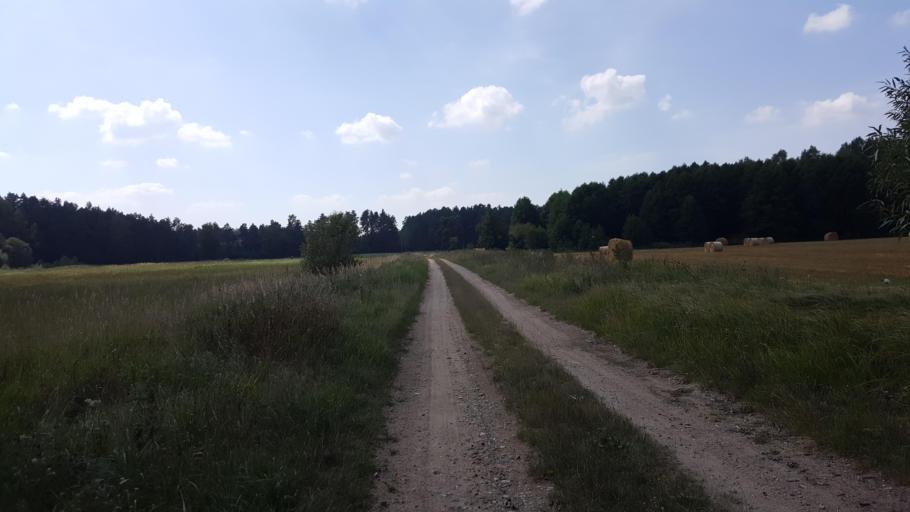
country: PL
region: Podlasie
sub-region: Powiat hajnowski
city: Hajnowka
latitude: 52.5739
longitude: 23.5648
